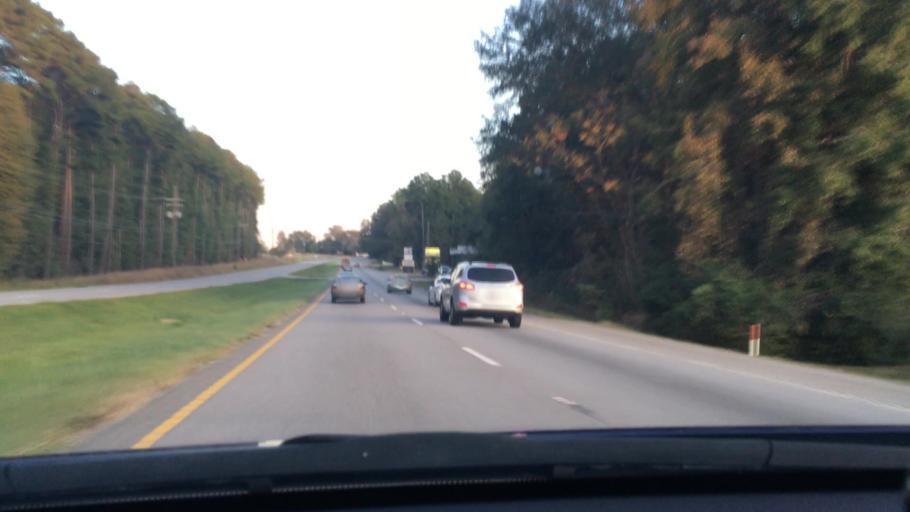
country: US
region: South Carolina
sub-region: Richland County
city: Hopkins
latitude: 33.9486
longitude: -80.8149
